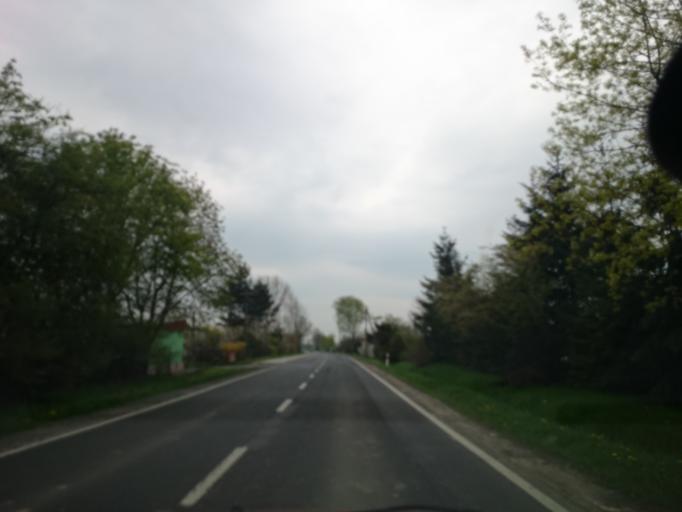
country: PL
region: Opole Voivodeship
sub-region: Powiat nyski
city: Glucholazy
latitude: 50.3195
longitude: 17.4296
